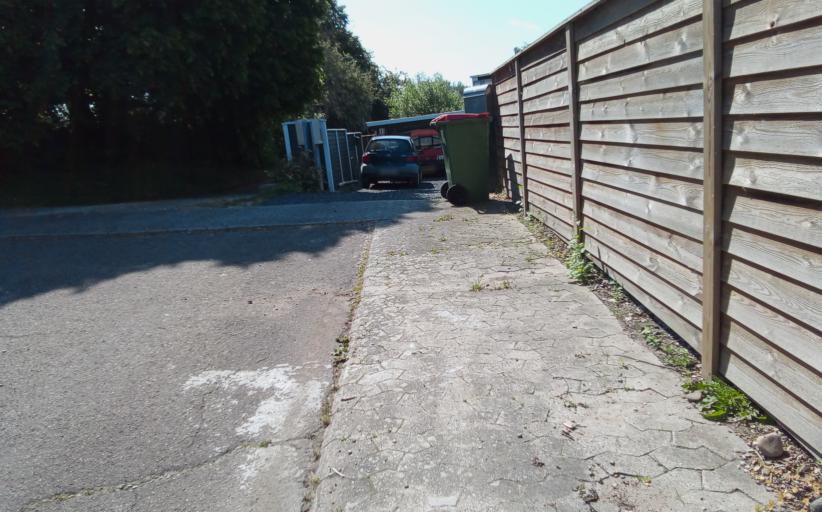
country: DK
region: Capital Region
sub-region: Gribskov Kommune
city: Helsinge
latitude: 56.0072
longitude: 12.1129
